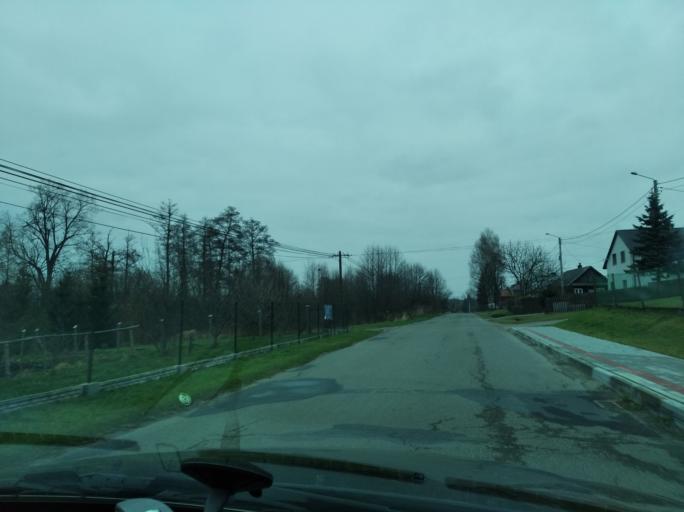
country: PL
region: Subcarpathian Voivodeship
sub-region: Powiat lancucki
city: Brzoza Stadnicka
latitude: 50.2007
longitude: 22.2893
